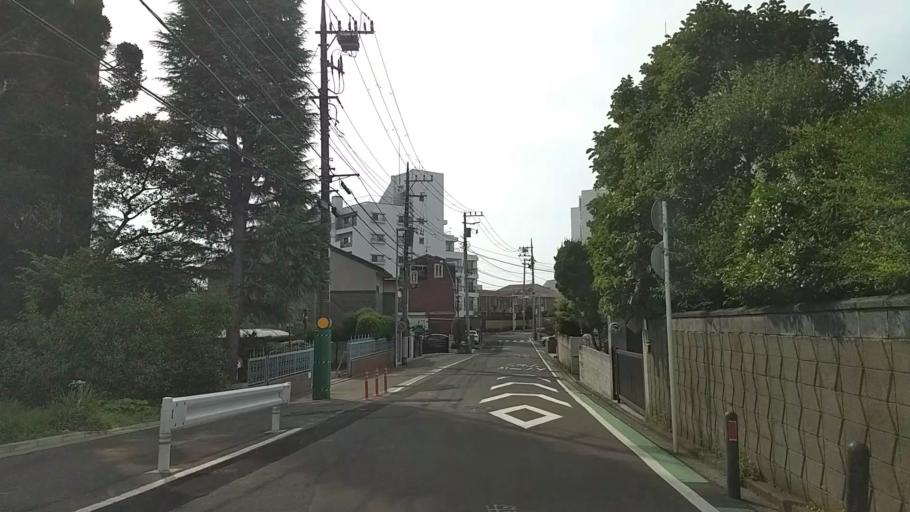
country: JP
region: Kanagawa
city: Yokohama
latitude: 35.4379
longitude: 139.6557
